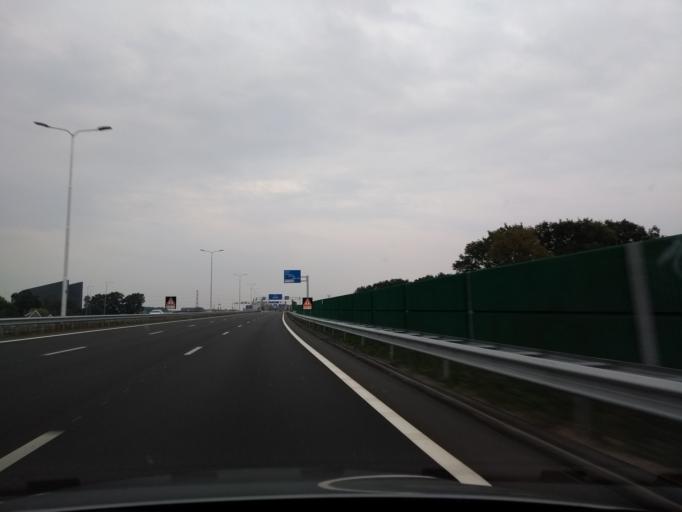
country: NL
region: Overijssel
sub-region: Gemeente Hengelo
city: Hengelo
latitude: 52.2019
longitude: 6.8198
